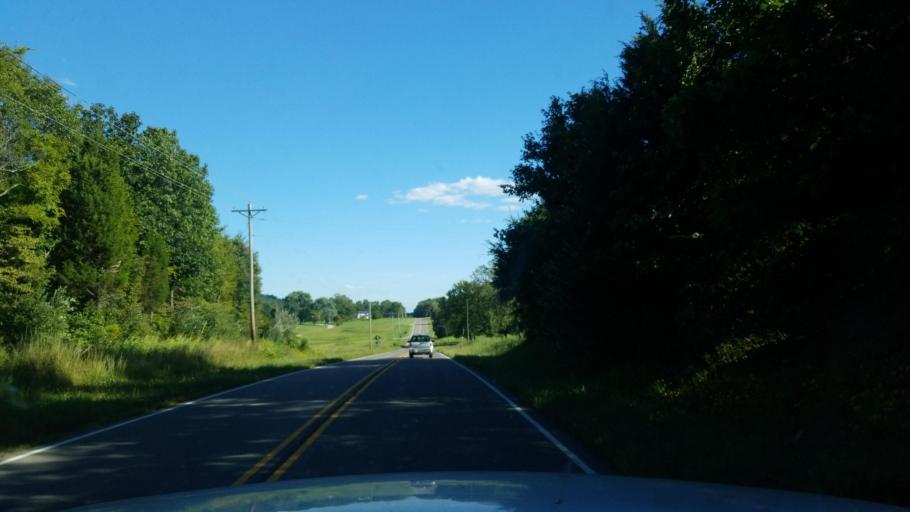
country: US
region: Illinois
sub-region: Saline County
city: Harrisburg
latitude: 37.6213
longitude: -88.4719
